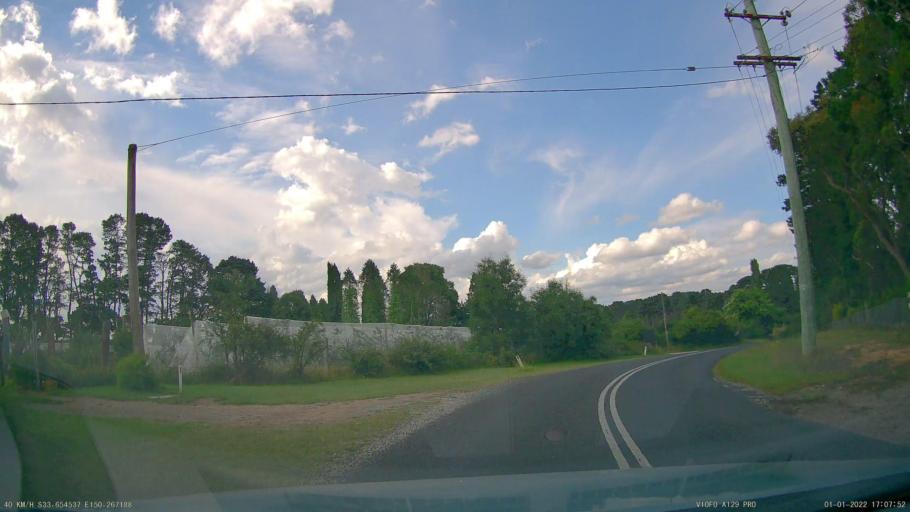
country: AU
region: New South Wales
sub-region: Blue Mountains Municipality
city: Blackheath
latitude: -33.6545
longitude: 150.2671
